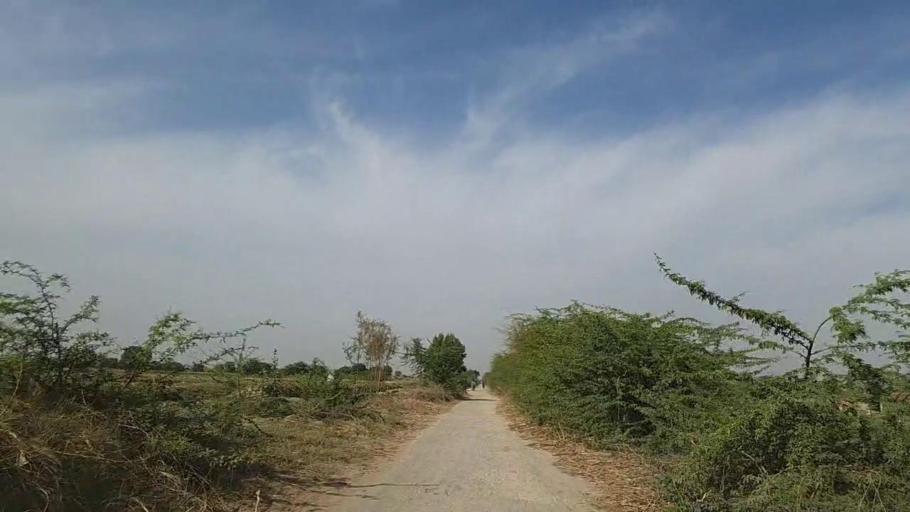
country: PK
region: Sindh
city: Samaro
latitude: 25.2352
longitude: 69.4240
